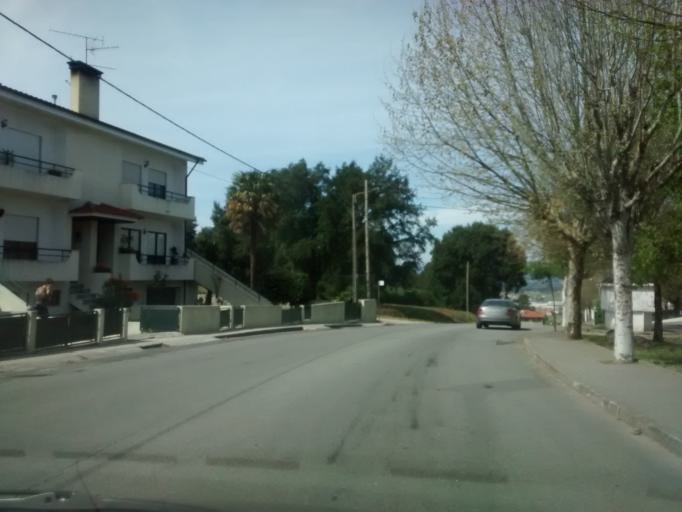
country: PT
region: Braga
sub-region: Braga
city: Braga
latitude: 41.5421
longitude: -8.4425
